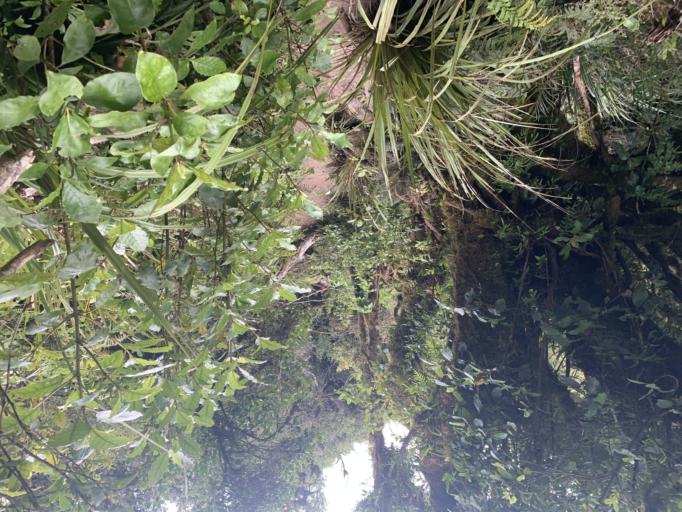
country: NZ
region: Waikato
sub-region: Taupo District
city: Taupo
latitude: -38.6957
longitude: 176.1606
